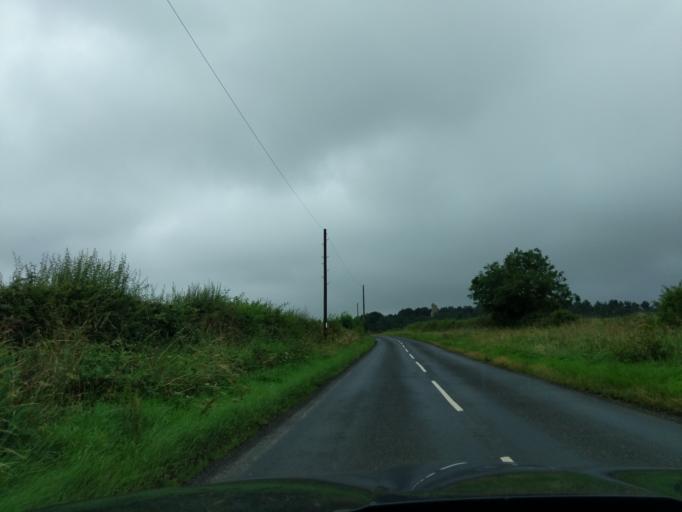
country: GB
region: England
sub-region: Northumberland
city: Ford
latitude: 55.6732
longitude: -2.1019
